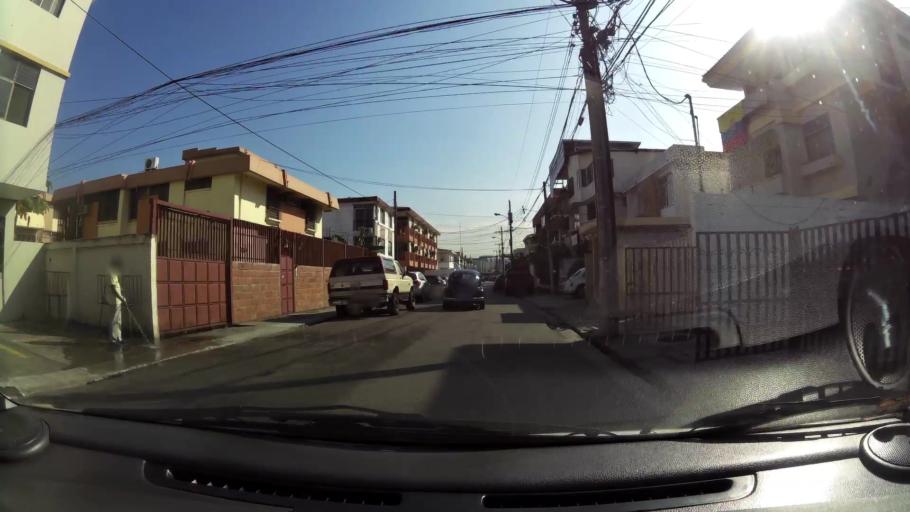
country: EC
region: Guayas
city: Guayaquil
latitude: -2.1742
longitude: -79.9010
